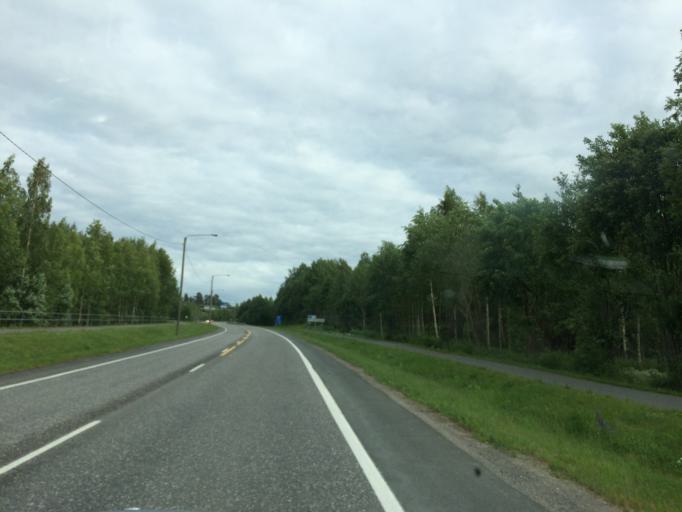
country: FI
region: Haeme
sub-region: Haemeenlinna
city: Haemeenlinna
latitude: 60.9687
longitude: 24.4780
